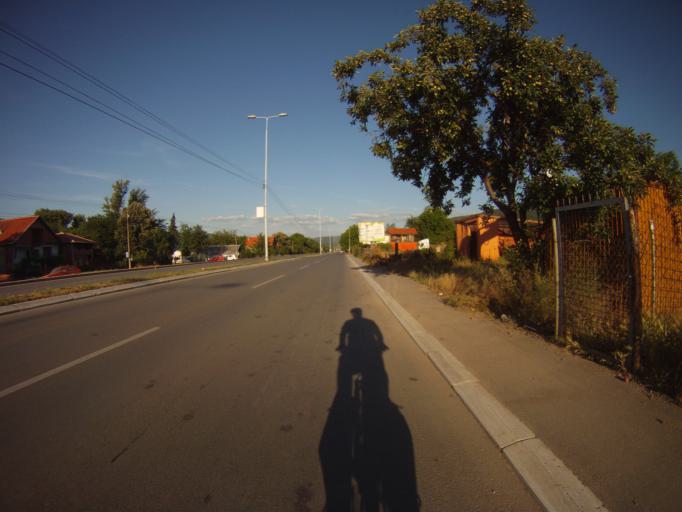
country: RS
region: Central Serbia
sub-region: Nisavski Okrug
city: Niska Banja
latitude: 43.3020
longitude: 21.9852
